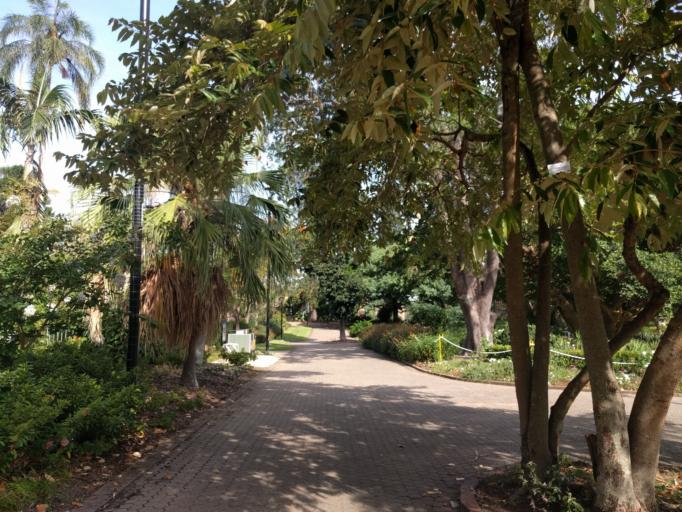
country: AU
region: Queensland
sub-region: Brisbane
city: Brisbane
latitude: -27.4744
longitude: 153.0302
